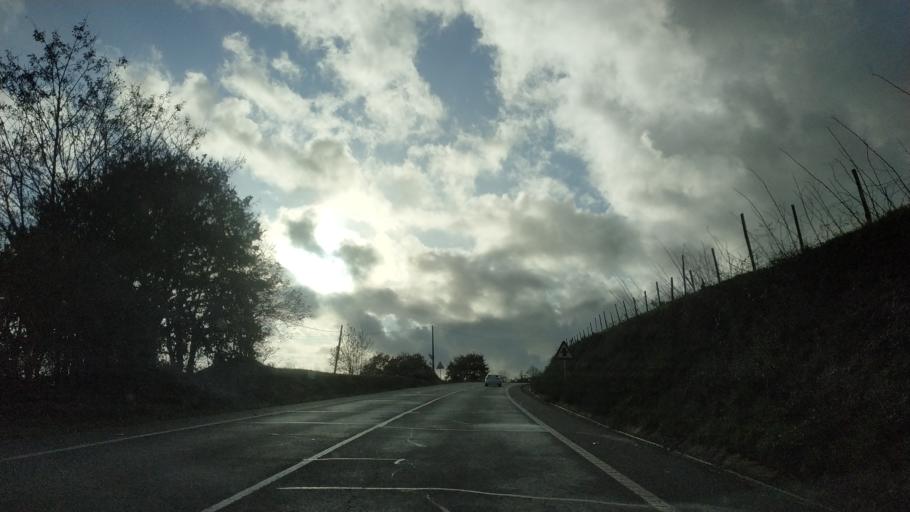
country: ES
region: Galicia
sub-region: Provincia da Coruna
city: Arzua
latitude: 42.8907
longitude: -8.1739
